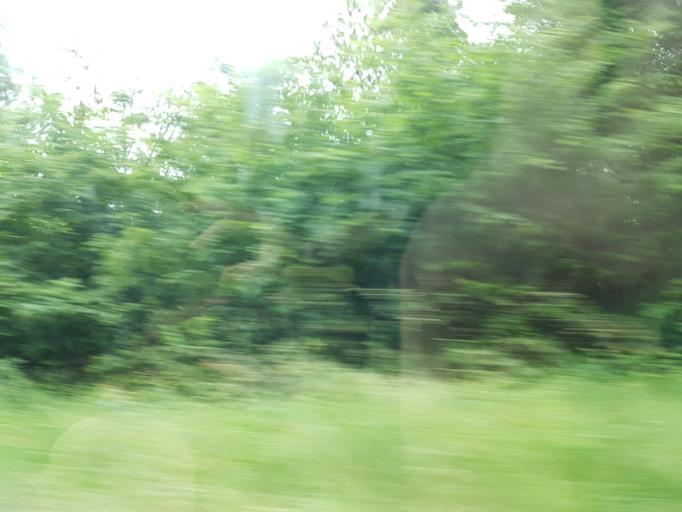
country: FR
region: Bourgogne
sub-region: Departement de la Nievre
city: Corbigny
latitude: 47.1943
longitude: 3.7254
